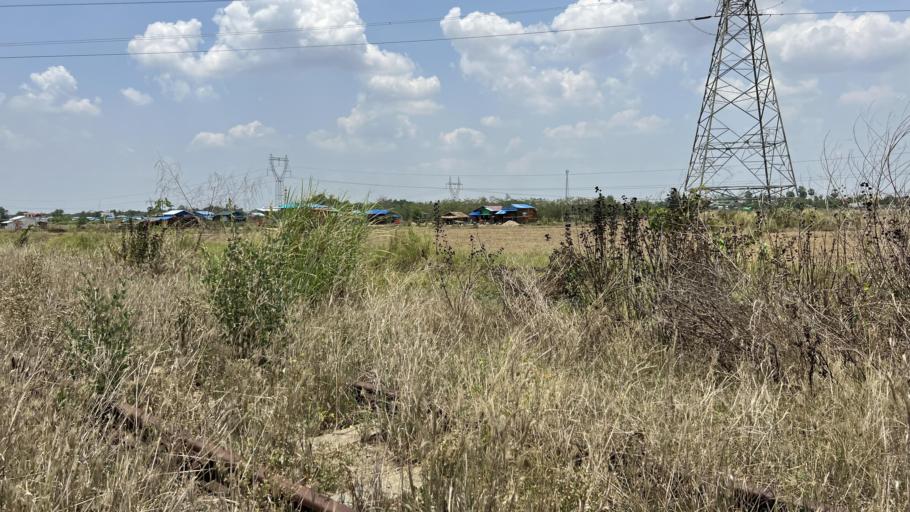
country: MM
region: Yangon
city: Kanbe
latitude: 16.8838
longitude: 95.9978
